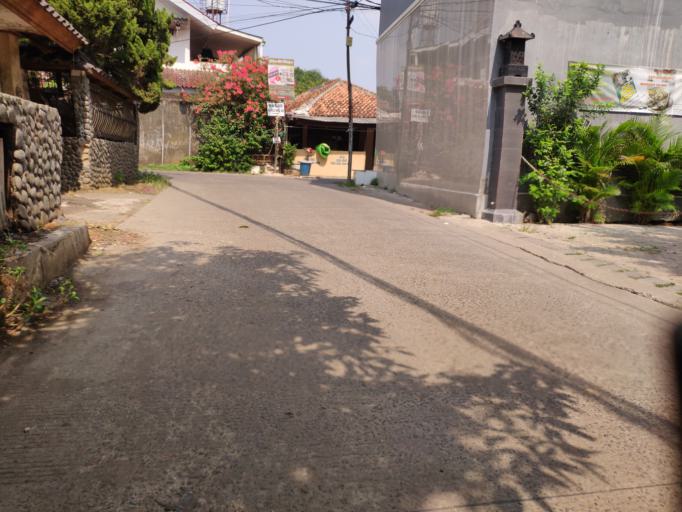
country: ID
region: West Java
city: Pamulang
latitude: -6.3255
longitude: 106.7986
